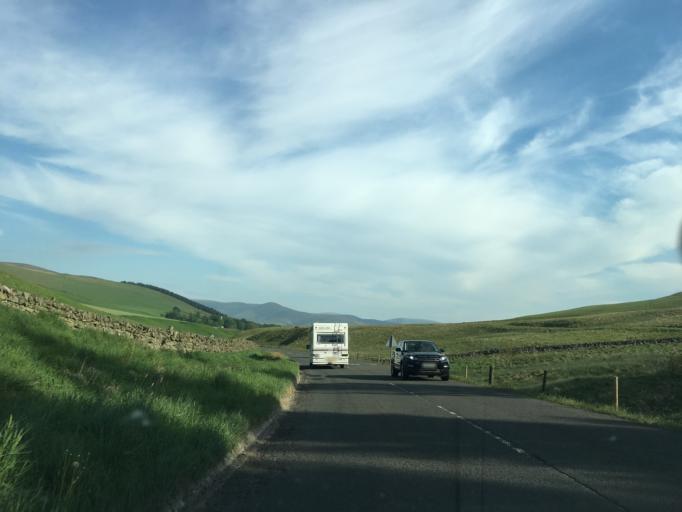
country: GB
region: Scotland
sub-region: South Lanarkshire
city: Biggar
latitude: 55.6367
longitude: -3.4257
